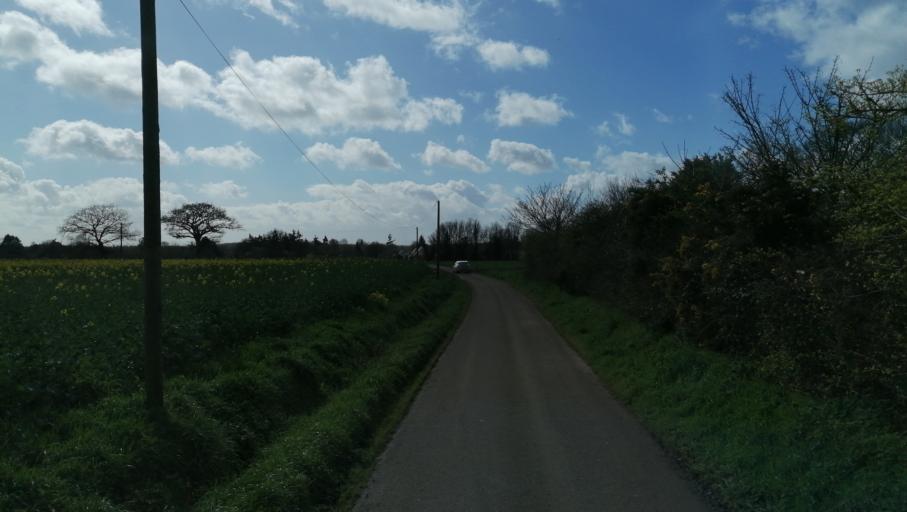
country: FR
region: Brittany
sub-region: Departement des Cotes-d'Armor
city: Pleguien
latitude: 48.6388
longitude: -2.9288
